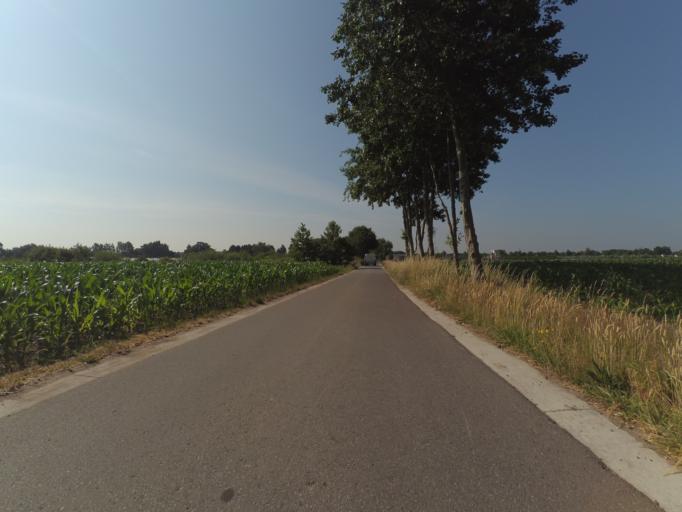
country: BE
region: Flanders
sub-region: Provincie Antwerpen
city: Essen
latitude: 51.4324
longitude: 4.4910
